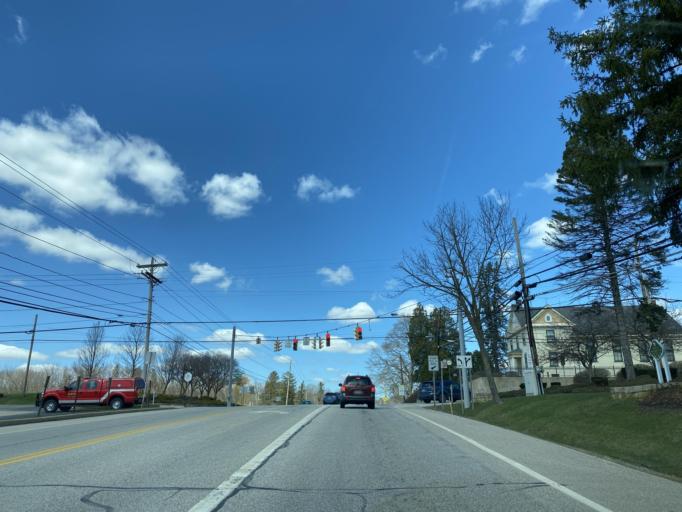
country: US
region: Ohio
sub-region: Summit County
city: Montrose-Ghent
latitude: 41.1685
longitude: -81.6368
